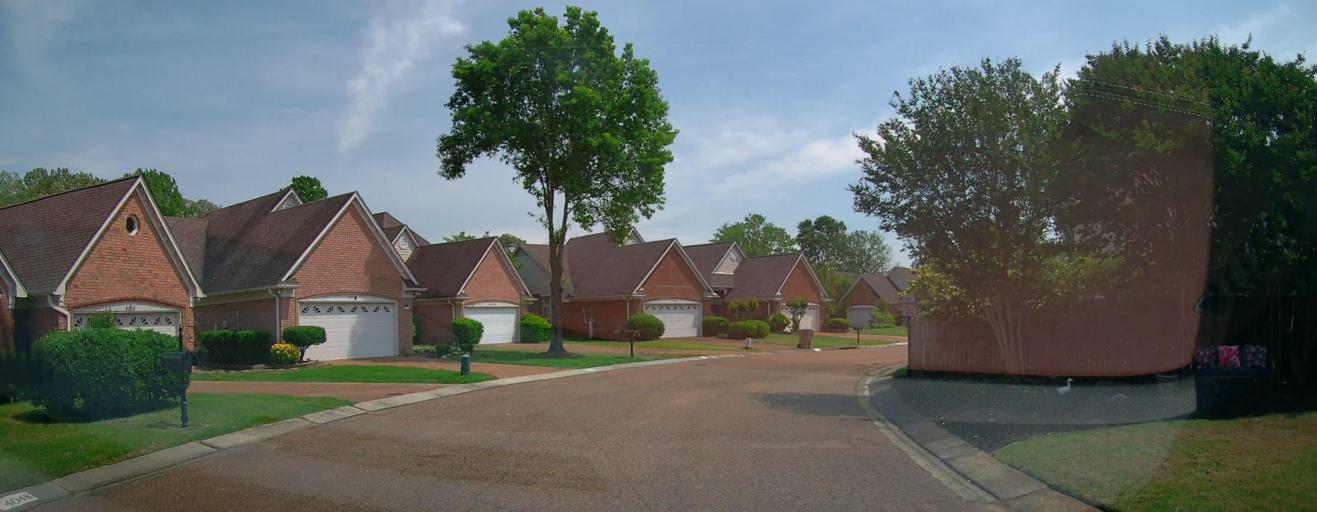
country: US
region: Tennessee
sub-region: Shelby County
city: Germantown
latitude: 35.0386
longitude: -89.7843
